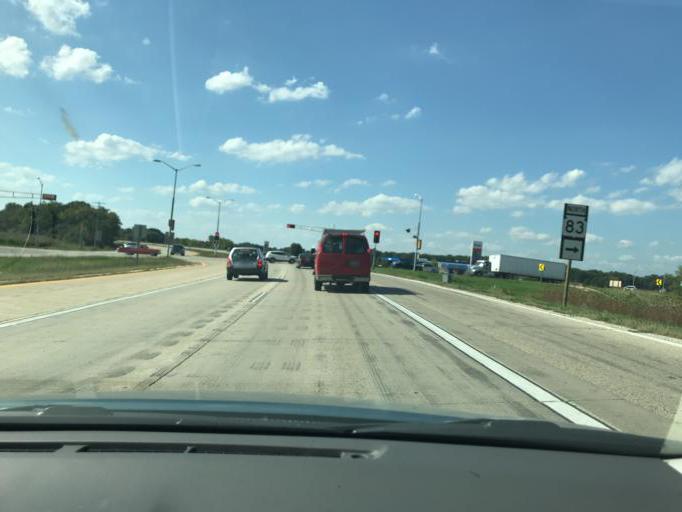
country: US
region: Wisconsin
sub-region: Kenosha County
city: Twin Lakes
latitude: 42.5819
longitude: -88.2171
